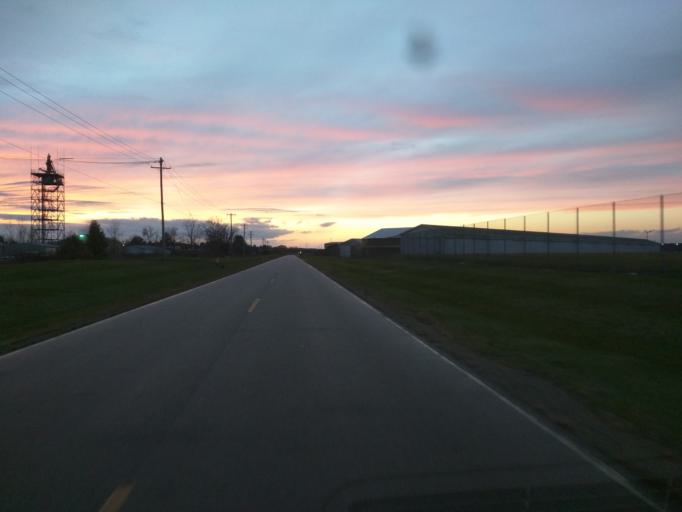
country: US
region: Michigan
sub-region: Ingham County
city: Edgemont Park
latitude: 42.7709
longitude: -84.5945
